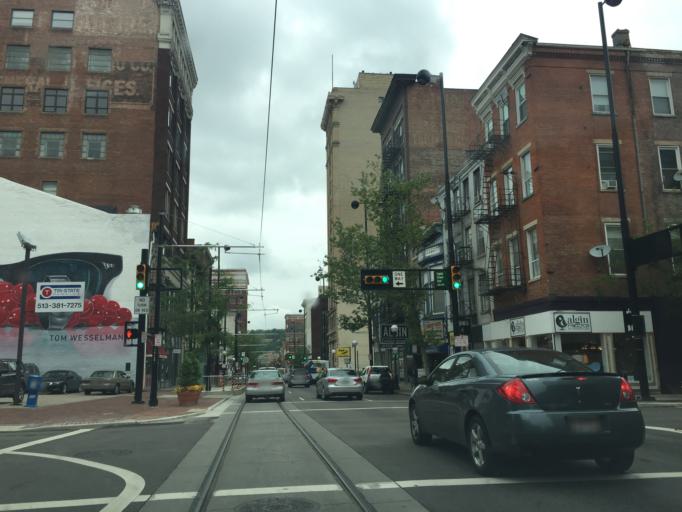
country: US
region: Kentucky
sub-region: Campbell County
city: Newport
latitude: 39.1048
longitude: -84.5105
